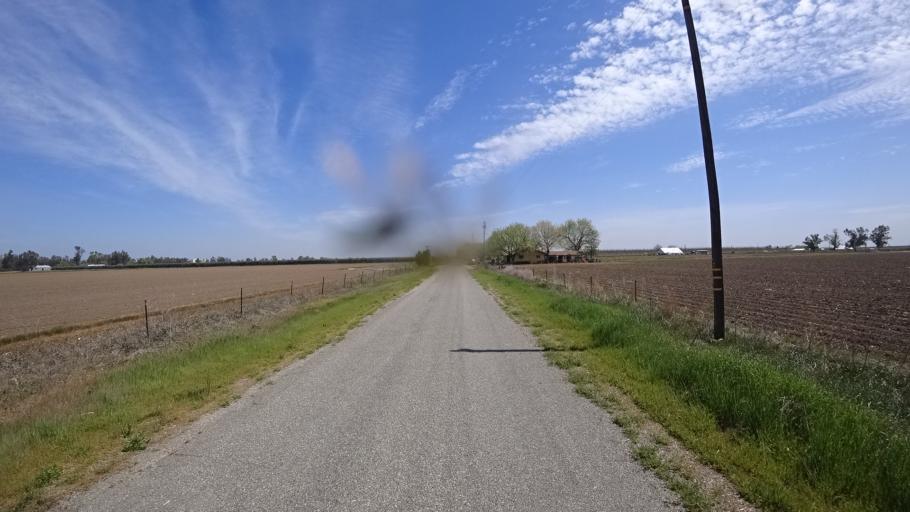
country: US
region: California
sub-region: Glenn County
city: Willows
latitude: 39.5769
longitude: -122.2023
